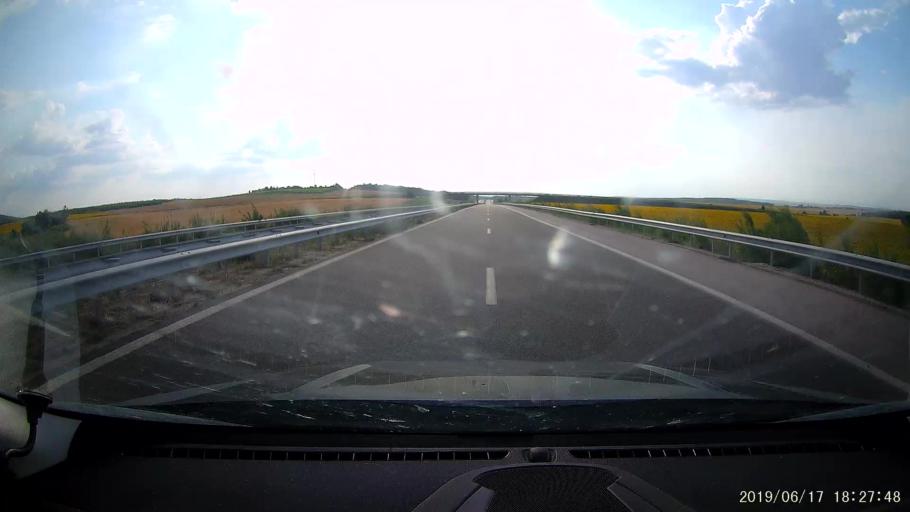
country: BG
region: Khaskovo
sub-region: Obshtina Dimitrovgrad
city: Dimitrovgrad
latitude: 42.0189
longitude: 25.5987
